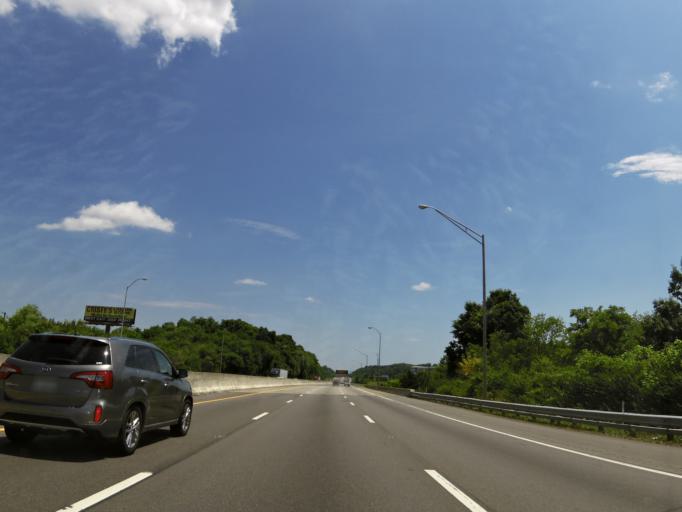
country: US
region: Tennessee
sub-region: Knox County
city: Knoxville
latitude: 36.0021
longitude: -83.8854
